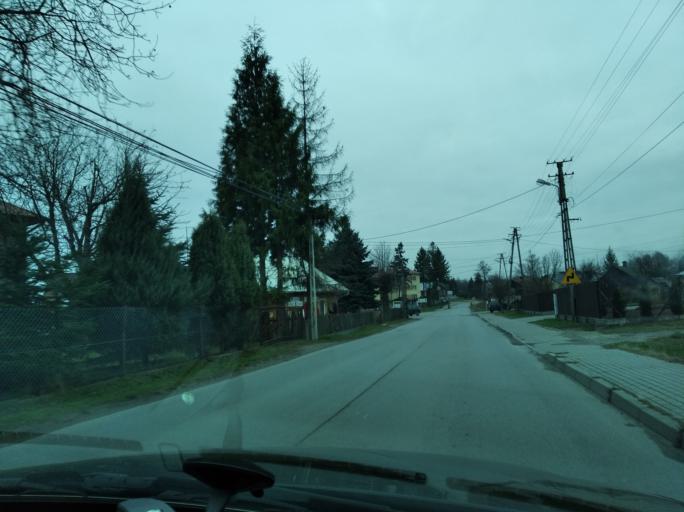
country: PL
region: Subcarpathian Voivodeship
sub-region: Powiat lancucki
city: Rakszawa
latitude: 50.1690
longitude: 22.2334
